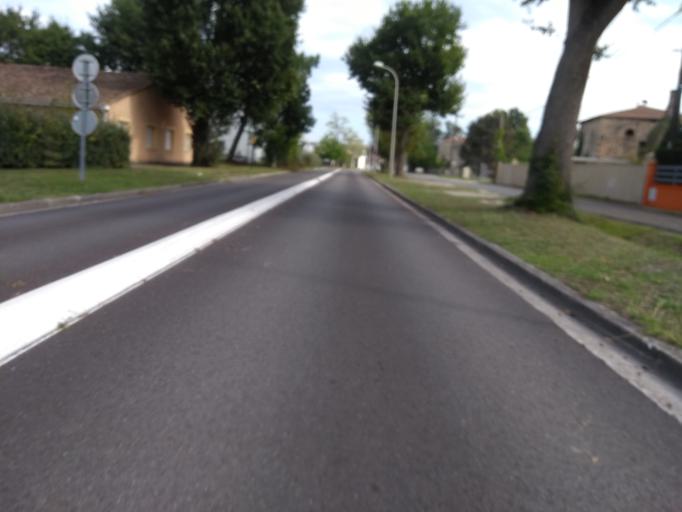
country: FR
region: Aquitaine
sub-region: Departement de la Gironde
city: Canejan
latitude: 44.7724
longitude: -0.6446
